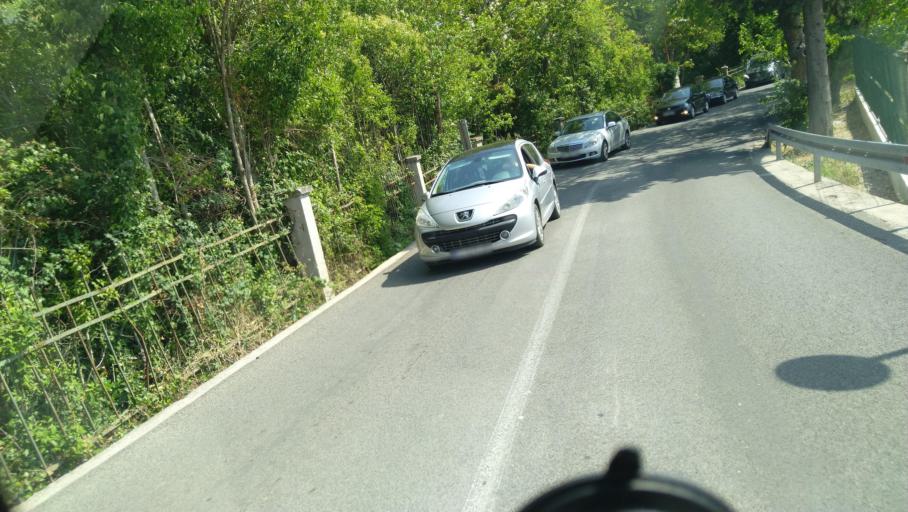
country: HR
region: Sibensko-Kniniska
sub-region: Grad Sibenik
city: Sibenik
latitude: 43.7196
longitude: 15.9066
